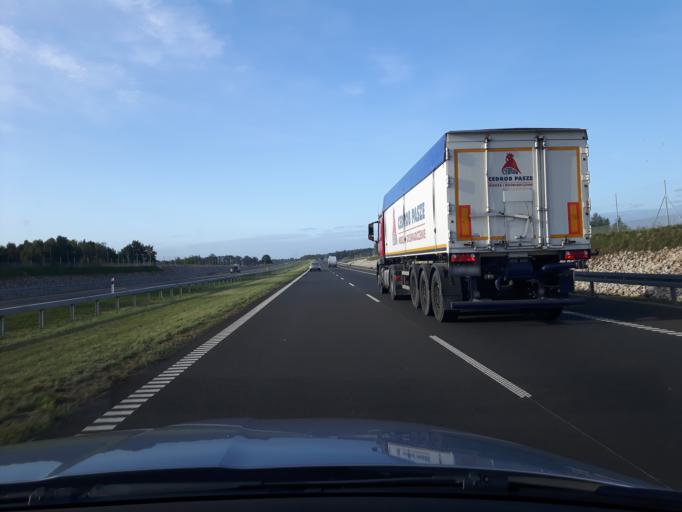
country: PL
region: Masovian Voivodeship
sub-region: Powiat radomski
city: Zakrzew
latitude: 51.4559
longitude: 21.0410
